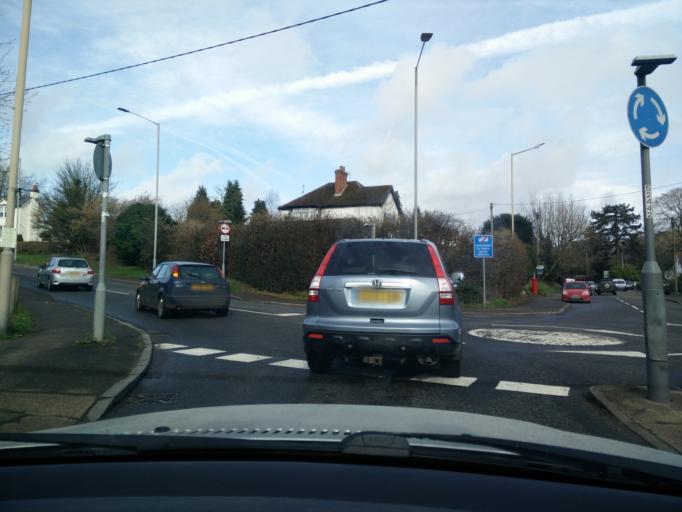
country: GB
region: England
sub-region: Buckinghamshire
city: High Wycombe
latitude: 51.6620
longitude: -0.7519
